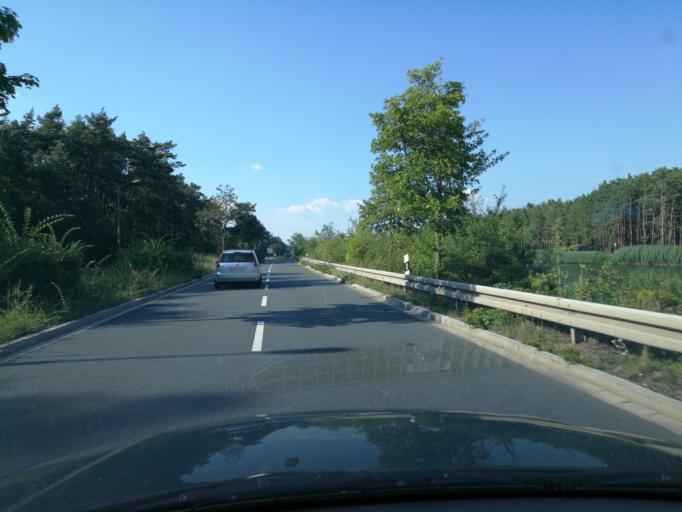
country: DE
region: Bavaria
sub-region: Regierungsbezirk Mittelfranken
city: Erlangen
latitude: 49.6035
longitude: 10.9717
